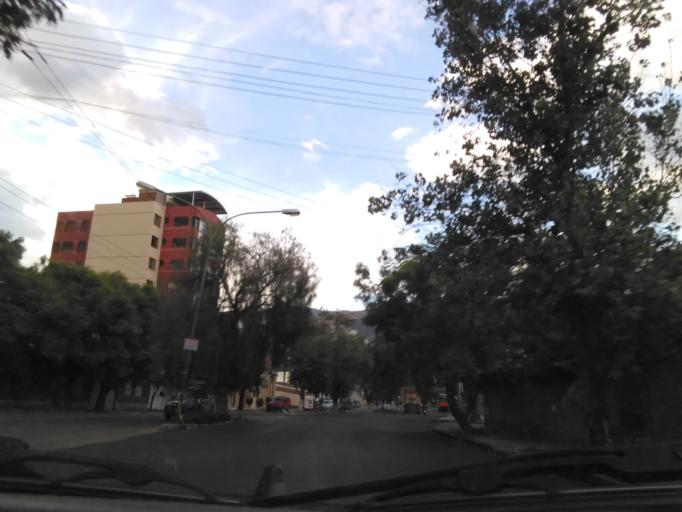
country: BO
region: Cochabamba
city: Cochabamba
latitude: -17.3681
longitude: -66.1758
